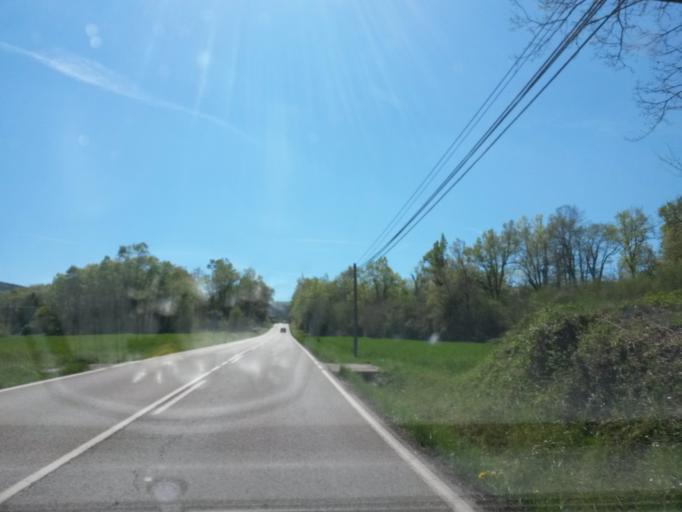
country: ES
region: Catalonia
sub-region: Provincia de Girona
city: Sant Cristofol de les Fonts
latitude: 42.1653
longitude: 2.5078
